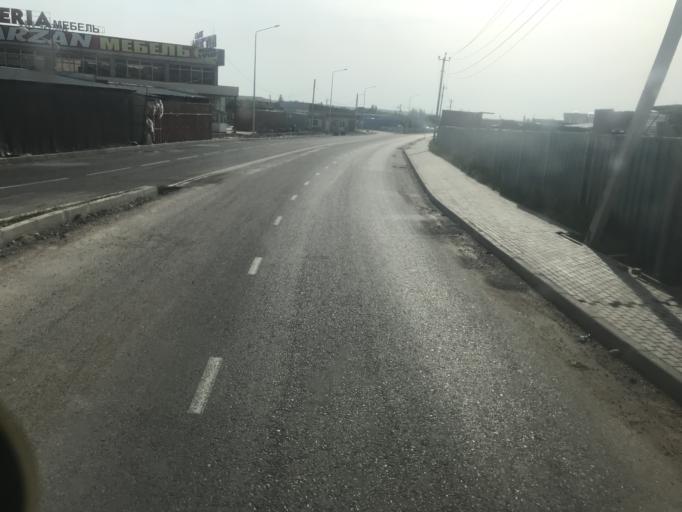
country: KZ
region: Ongtustik Qazaqstan
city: Shymkent
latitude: 42.3541
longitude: 69.5319
